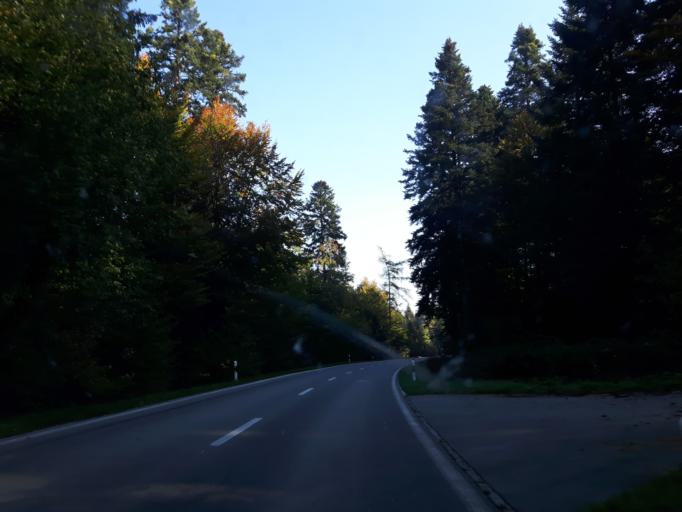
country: CH
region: Bern
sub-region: Oberaargau
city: Roggwil
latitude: 47.2496
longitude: 7.8458
